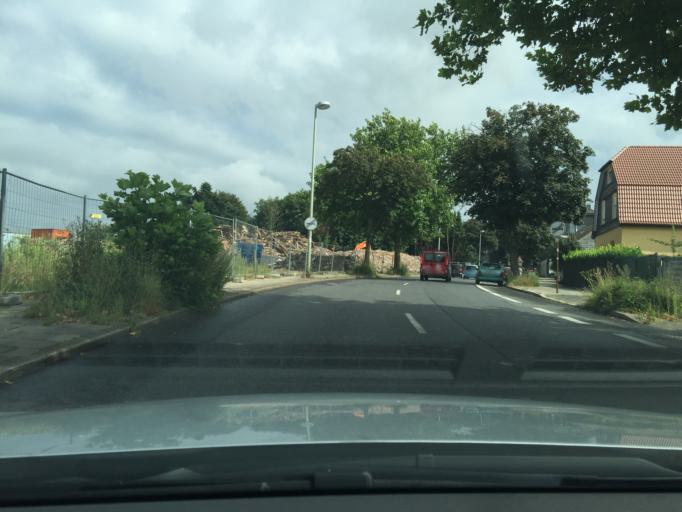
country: DE
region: North Rhine-Westphalia
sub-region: Regierungsbezirk Dusseldorf
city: Heiligenhaus
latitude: 51.3299
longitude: 7.0037
